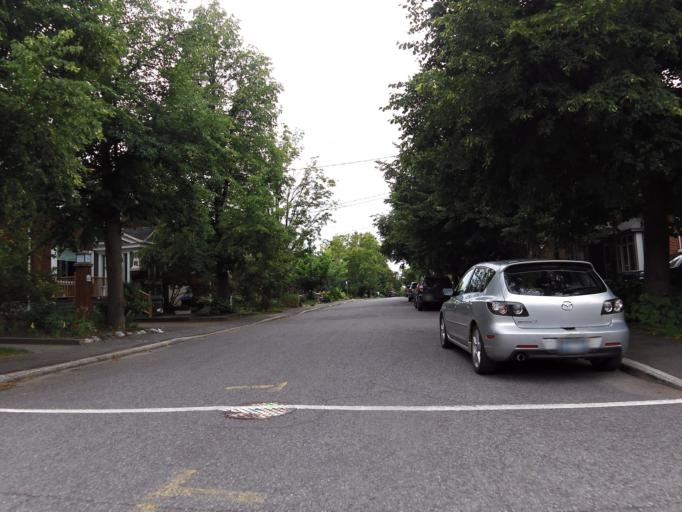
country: CA
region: Ontario
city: Ottawa
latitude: 45.3910
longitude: -75.6873
